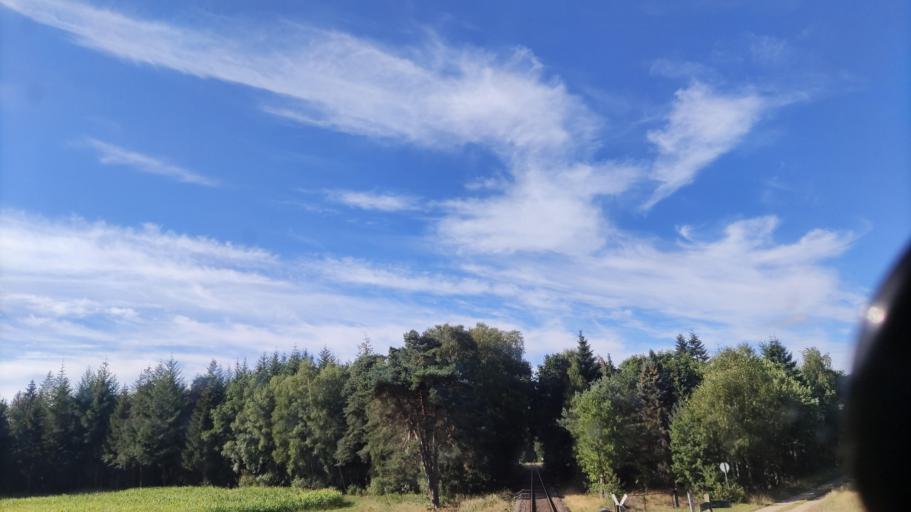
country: DE
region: Lower Saxony
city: Bispingen
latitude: 53.0402
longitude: 9.9383
